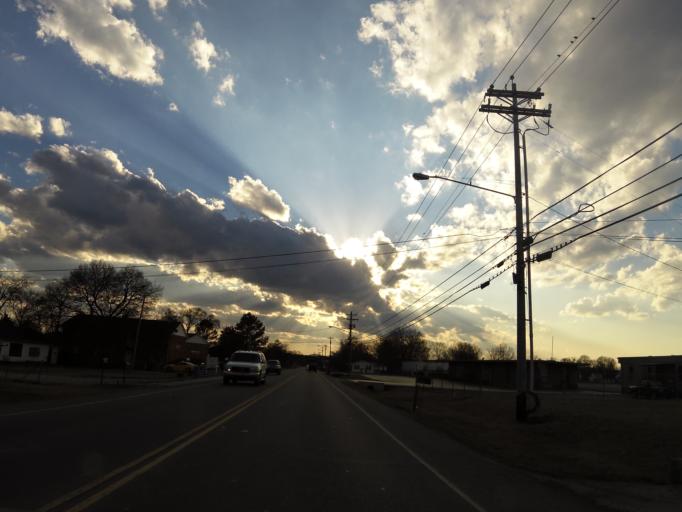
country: US
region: Tennessee
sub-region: Wilson County
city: Lebanon
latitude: 36.2116
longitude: -86.2708
